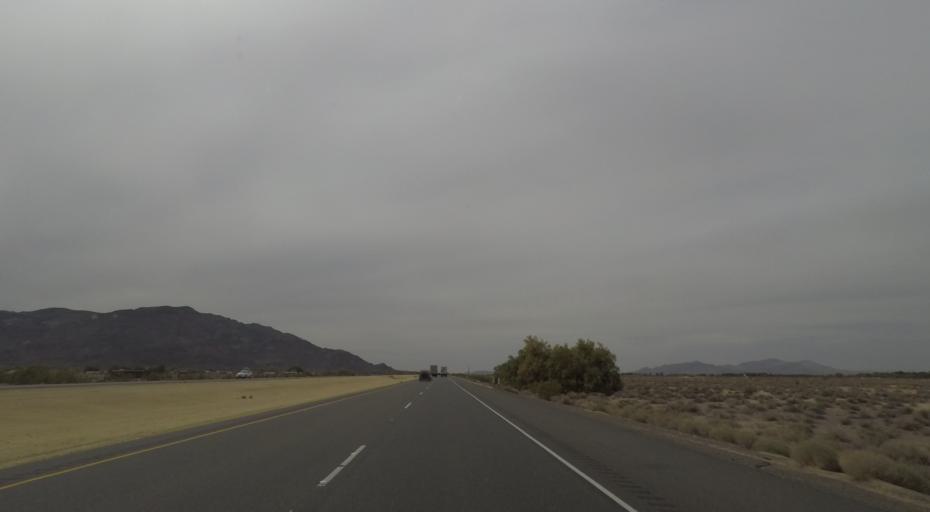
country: US
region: California
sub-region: San Bernardino County
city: Barstow
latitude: 34.8204
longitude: -116.6315
